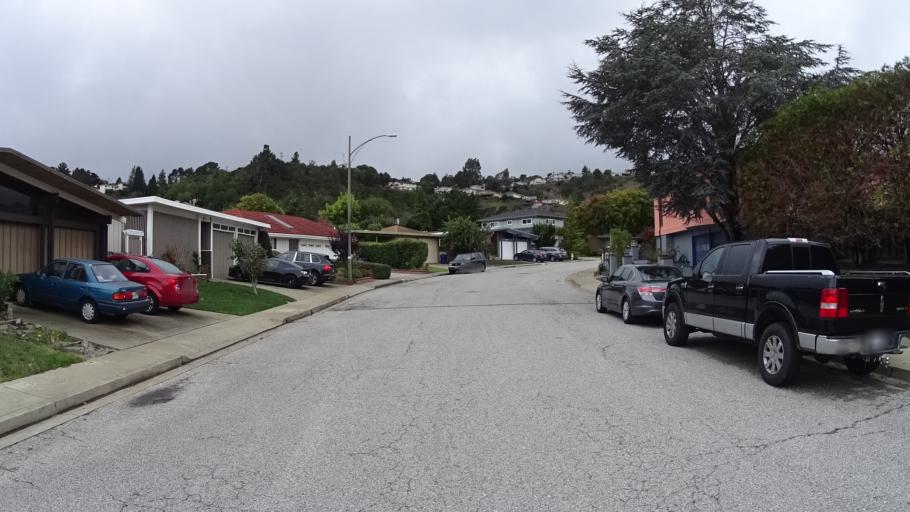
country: US
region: California
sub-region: San Mateo County
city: Millbrae
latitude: 37.6000
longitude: -122.4138
